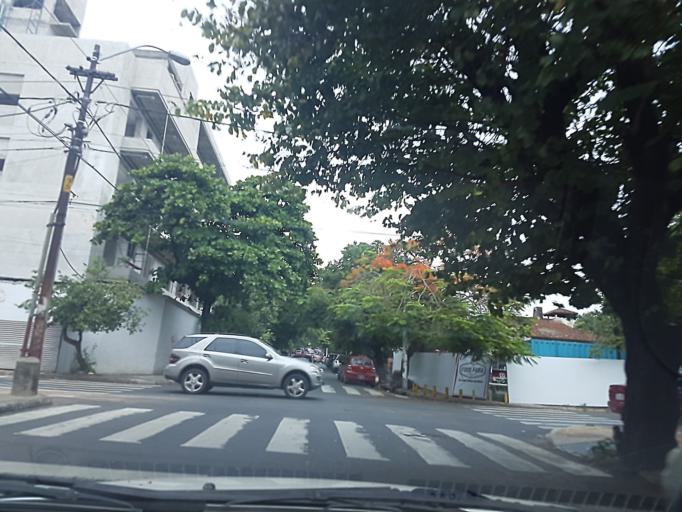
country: PY
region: Asuncion
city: Asuncion
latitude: -25.2946
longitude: -57.6144
